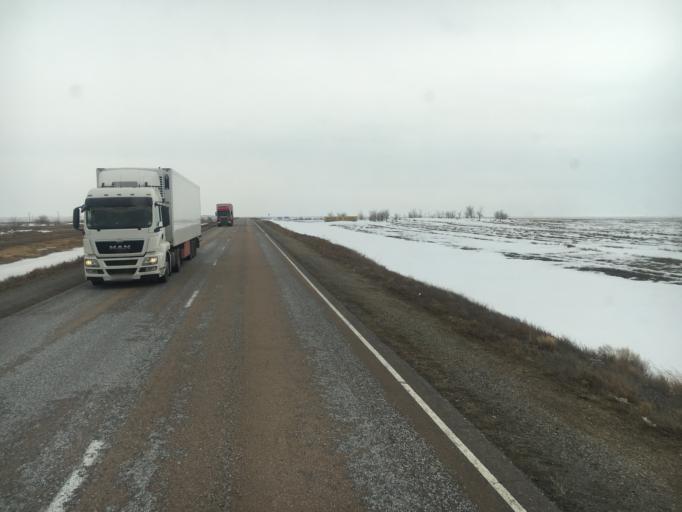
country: RU
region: Orenburg
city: Dombarovskiy
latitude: 50.0938
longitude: 59.4881
